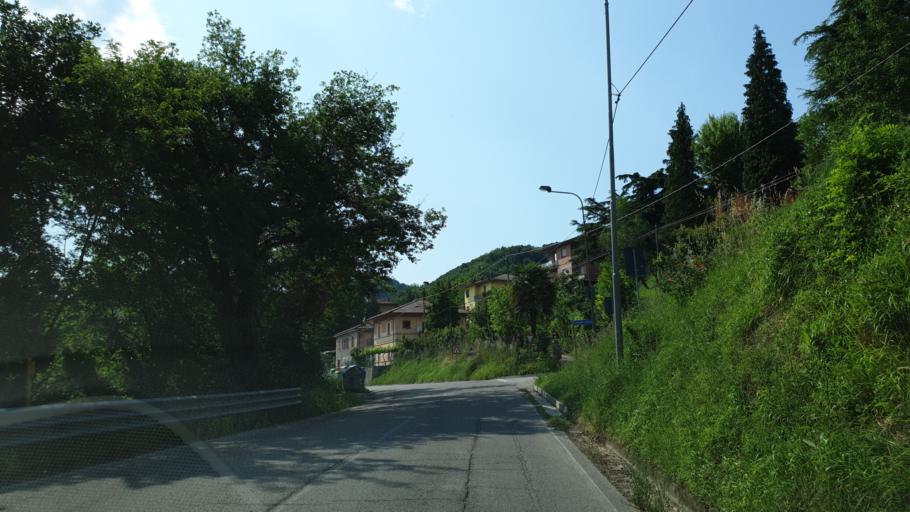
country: IT
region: Emilia-Romagna
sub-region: Forli-Cesena
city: Sarsina
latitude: 43.9241
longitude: 12.1581
